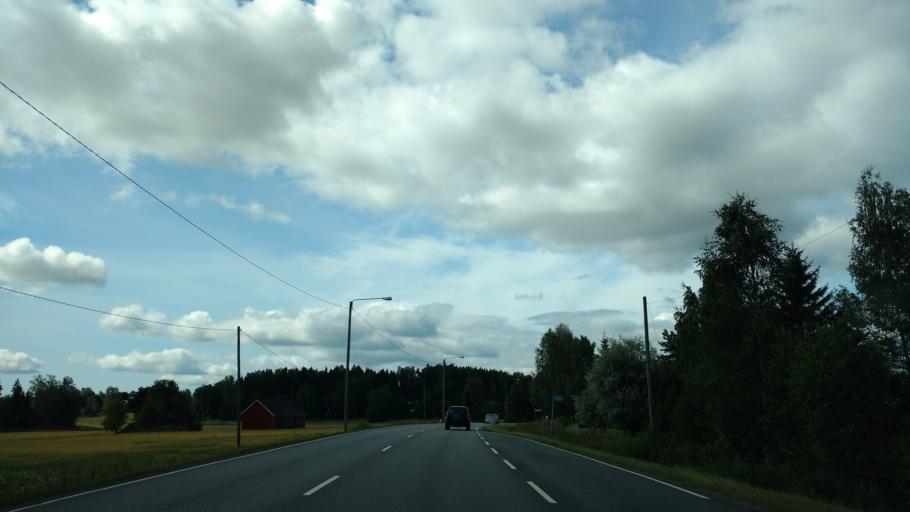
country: FI
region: Varsinais-Suomi
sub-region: Salo
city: Pernioe
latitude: 60.1744
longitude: 23.0344
